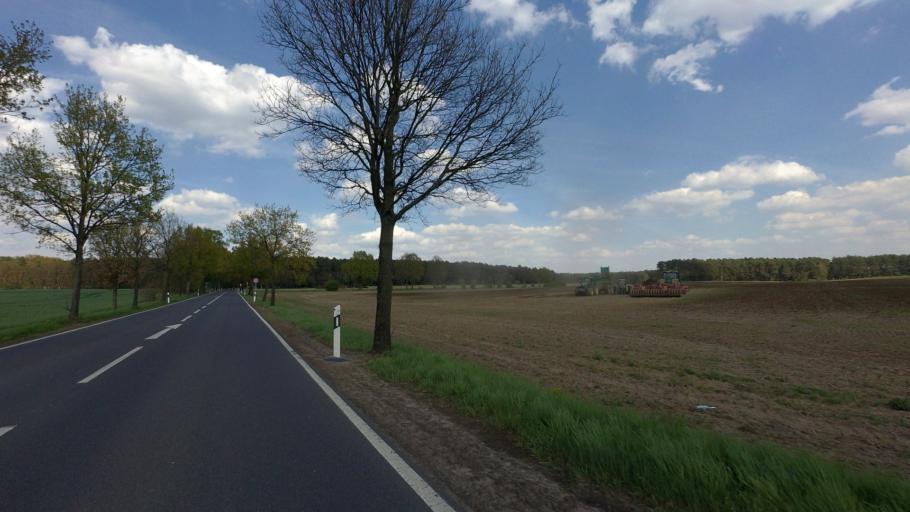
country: DE
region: Brandenburg
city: Marienwerder
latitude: 52.8772
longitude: 13.5423
